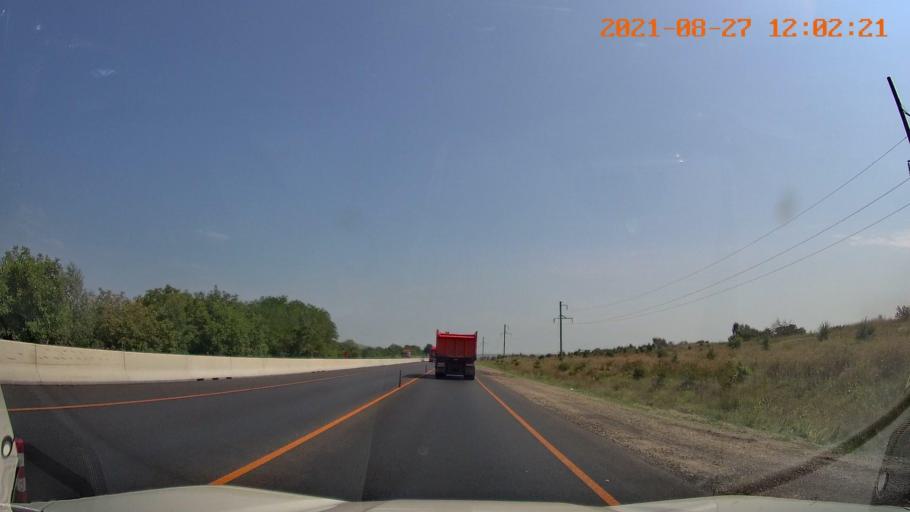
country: RU
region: Stavropol'skiy
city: Tatarka
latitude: 44.9516
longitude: 41.9482
